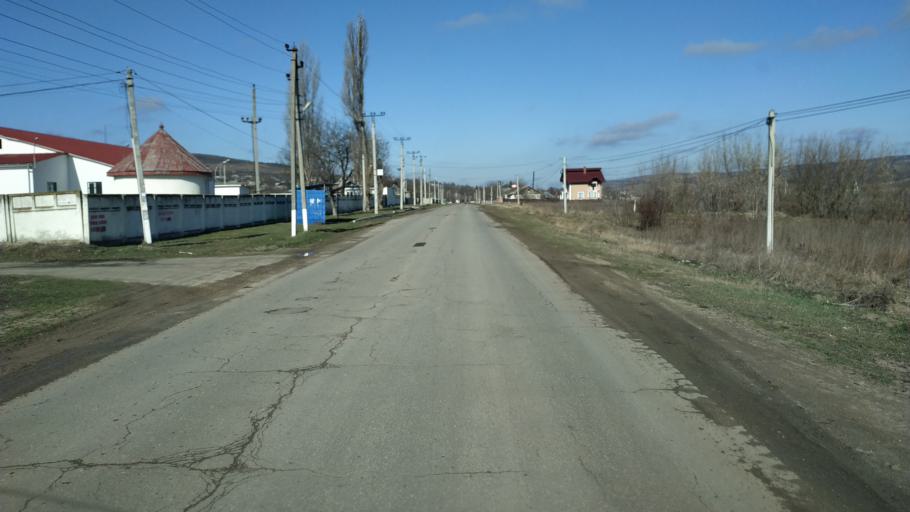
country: MD
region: Hincesti
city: Hincesti
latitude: 46.9524
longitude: 28.6104
